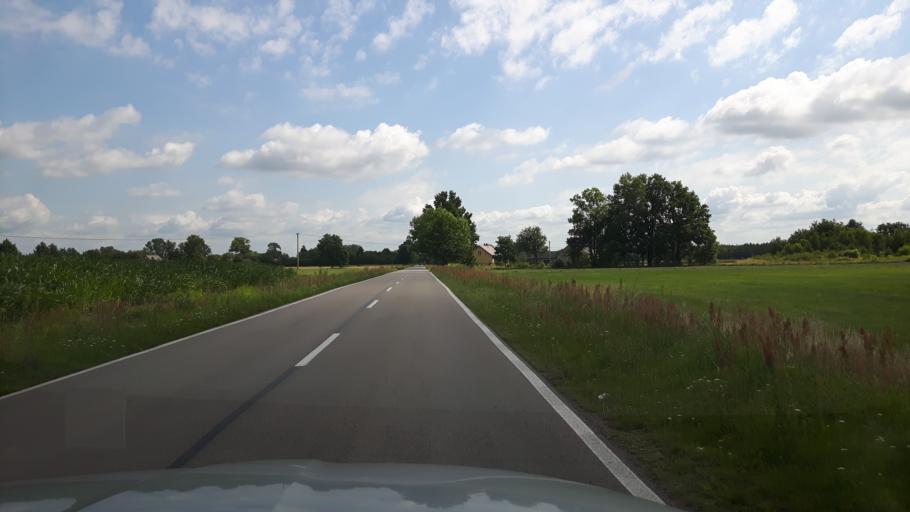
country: PL
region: Masovian Voivodeship
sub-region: Powiat wolominski
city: Strachowka
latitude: 52.4363
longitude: 21.5530
